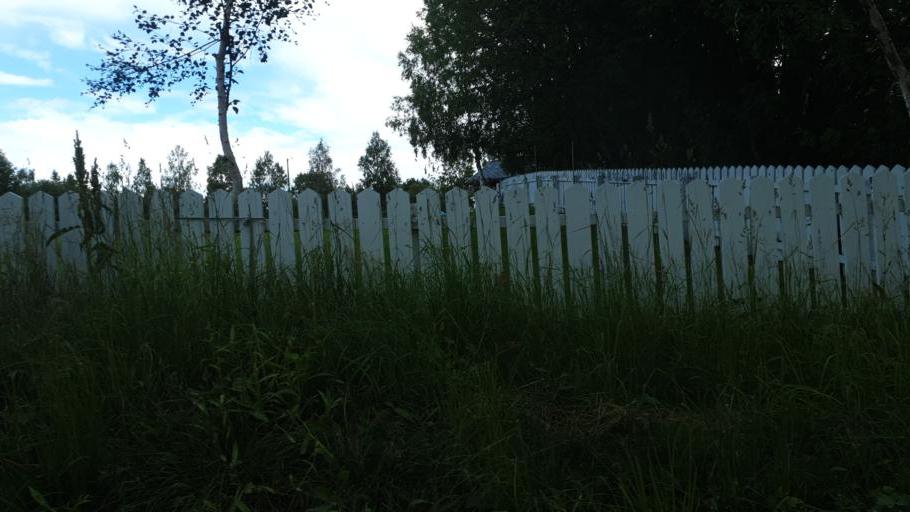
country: NO
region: Sor-Trondelag
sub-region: Rennebu
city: Berkak
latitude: 62.8297
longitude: 10.0035
